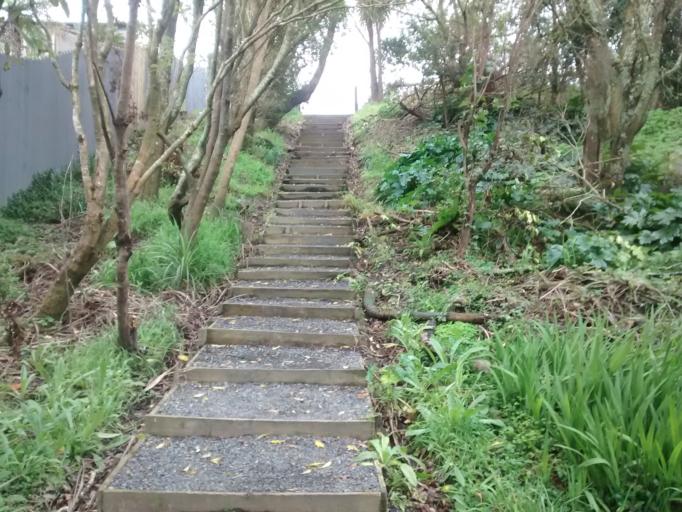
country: NZ
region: Auckland
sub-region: Auckland
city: Auckland
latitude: -36.8639
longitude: 174.7294
